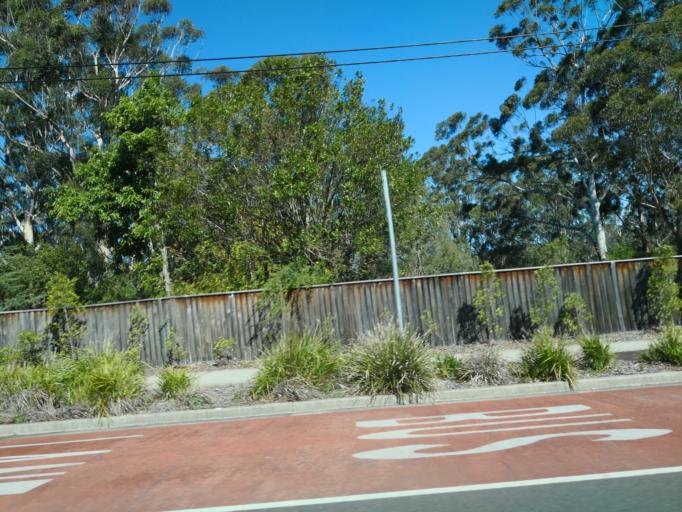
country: AU
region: New South Wales
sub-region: Gosford Shire
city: Erina
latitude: -33.4261
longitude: 151.3988
